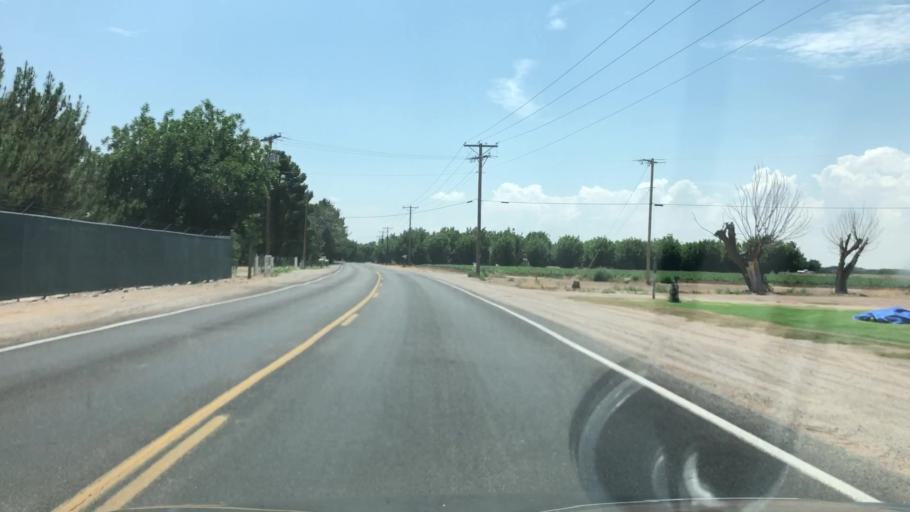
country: US
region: New Mexico
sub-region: Dona Ana County
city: La Union
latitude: 31.9527
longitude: -106.6441
